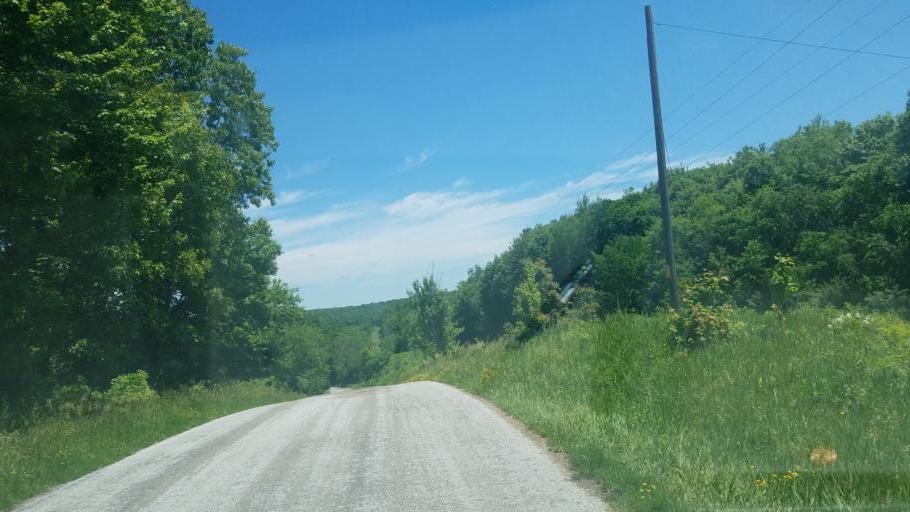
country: US
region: Ohio
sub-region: Coshocton County
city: Coshocton
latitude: 40.2675
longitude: -81.9590
